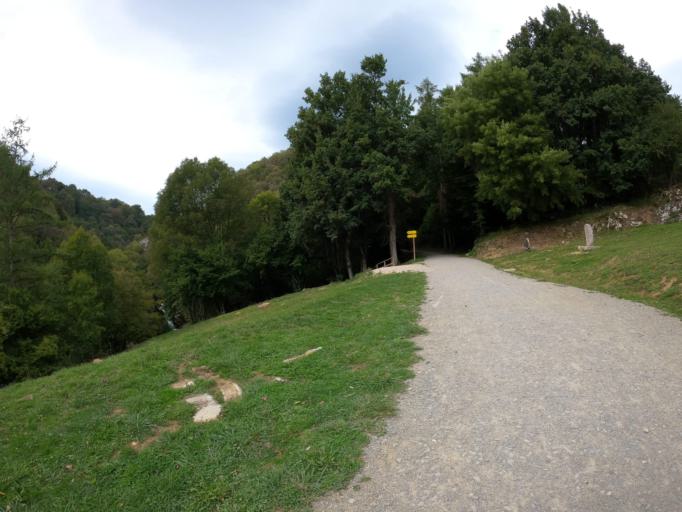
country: ES
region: Navarre
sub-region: Provincia de Navarra
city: Lekunberri
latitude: 42.9877
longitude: -1.8822
